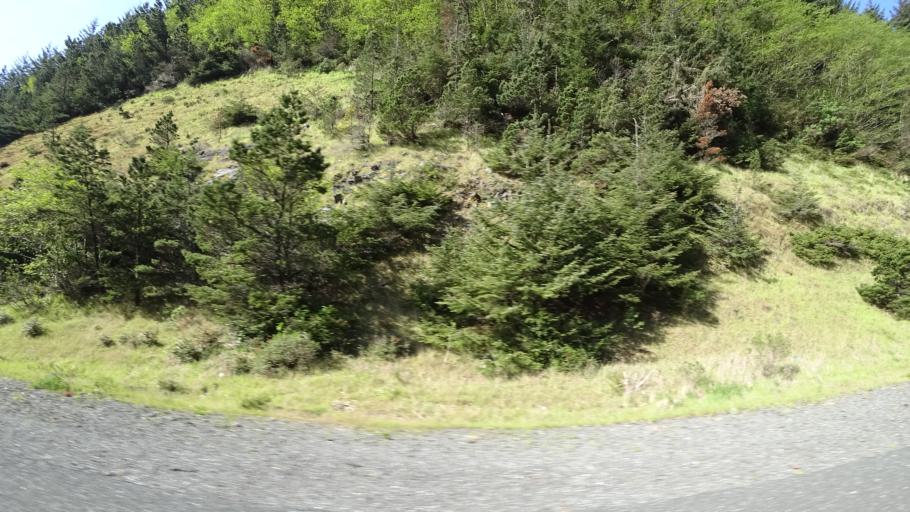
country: US
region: Oregon
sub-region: Curry County
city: Brookings
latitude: 42.1479
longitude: -124.3561
